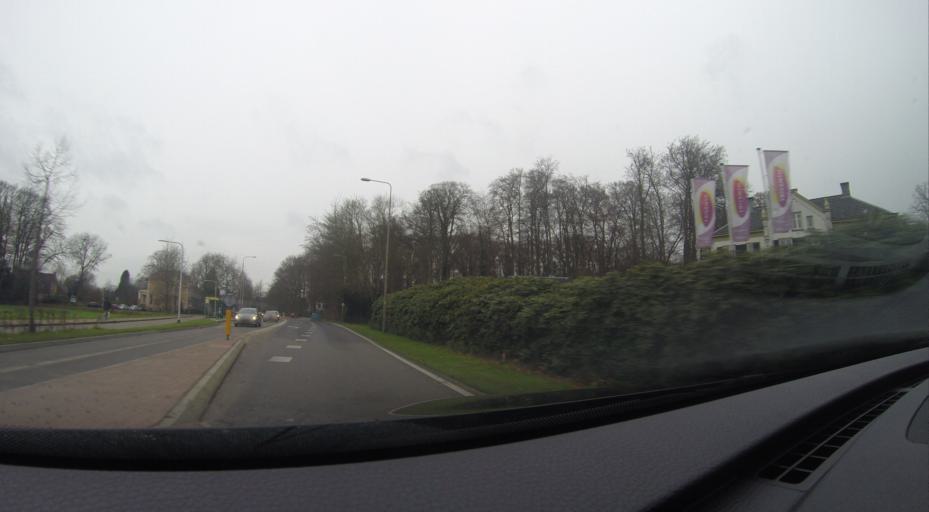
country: NL
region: Gelderland
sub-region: Gemeente Zutphen
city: Warnsveld
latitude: 52.1444
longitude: 6.2347
